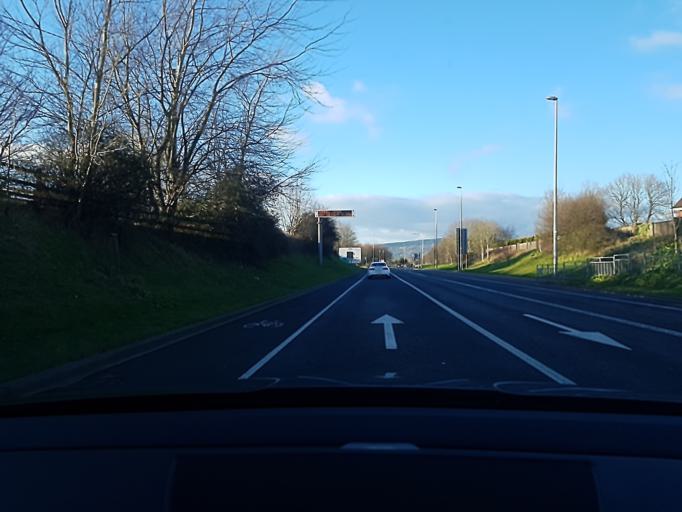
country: IE
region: Munster
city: Moyross
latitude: 52.6635
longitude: -8.6679
